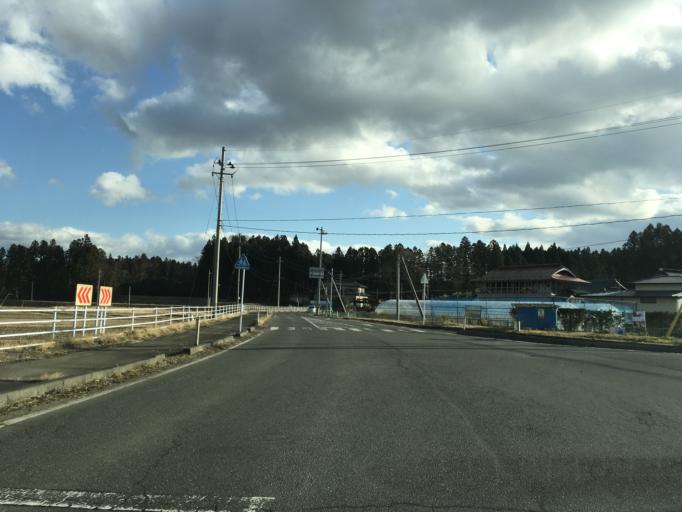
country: JP
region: Iwate
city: Ichinoseki
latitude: 38.8210
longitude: 141.0028
